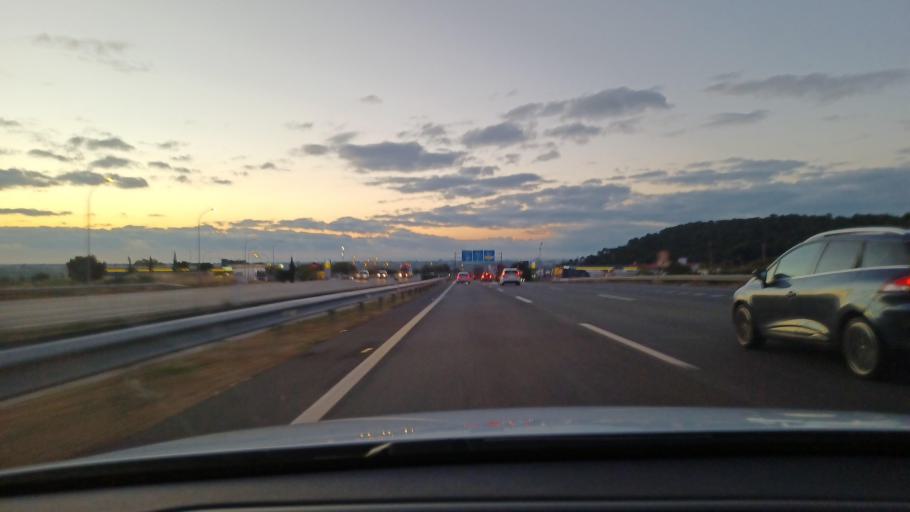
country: ES
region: Valencia
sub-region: Provincia de Valencia
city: Petres
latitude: 39.6530
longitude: -0.3037
